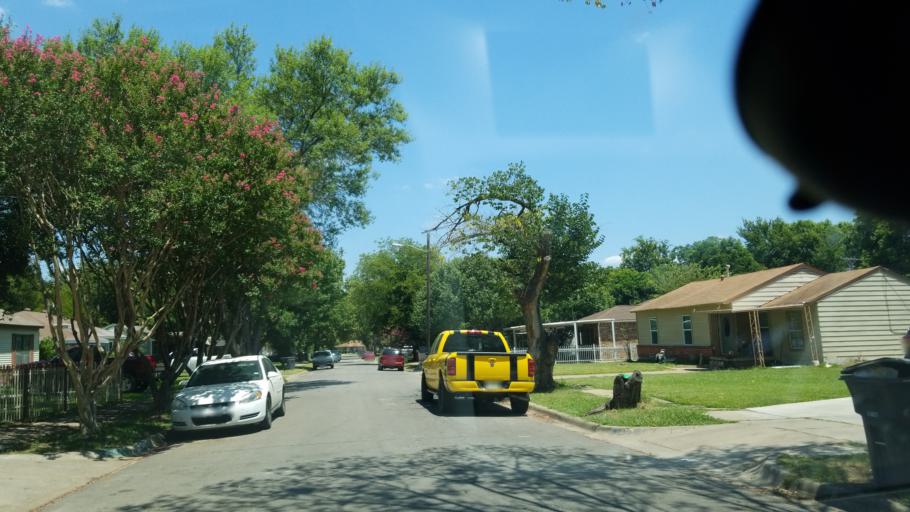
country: US
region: Texas
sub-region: Dallas County
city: Cockrell Hill
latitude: 32.7139
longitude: -96.8424
